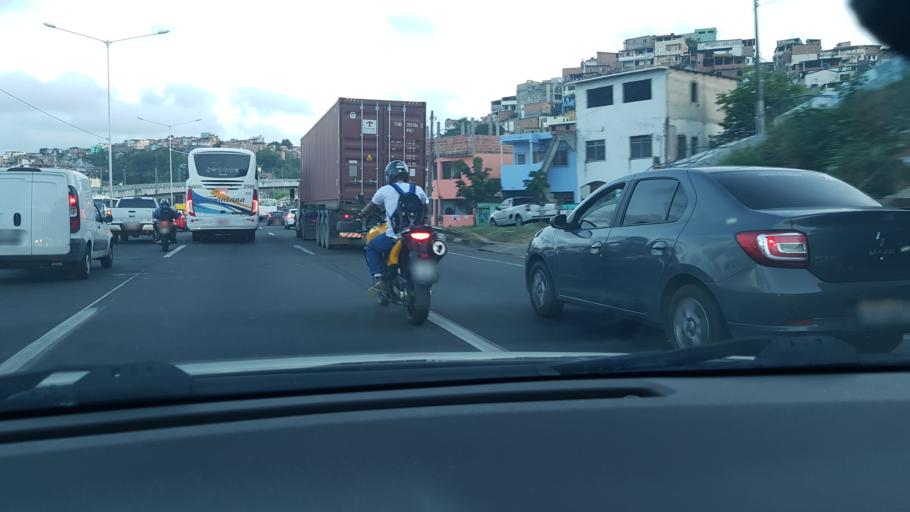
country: BR
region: Bahia
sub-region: Salvador
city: Salvador
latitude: -12.9402
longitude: -38.4714
